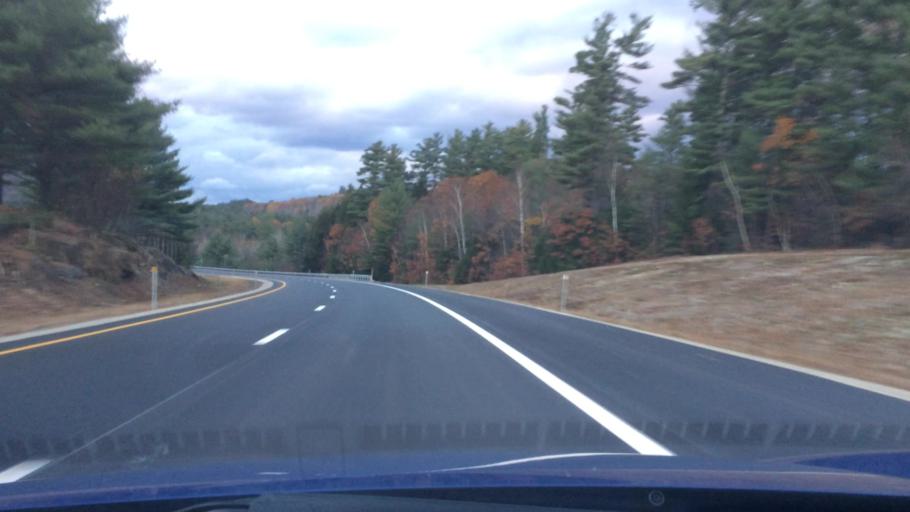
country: US
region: New Hampshire
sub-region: Grafton County
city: Thornton
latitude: 43.9300
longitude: -71.6865
